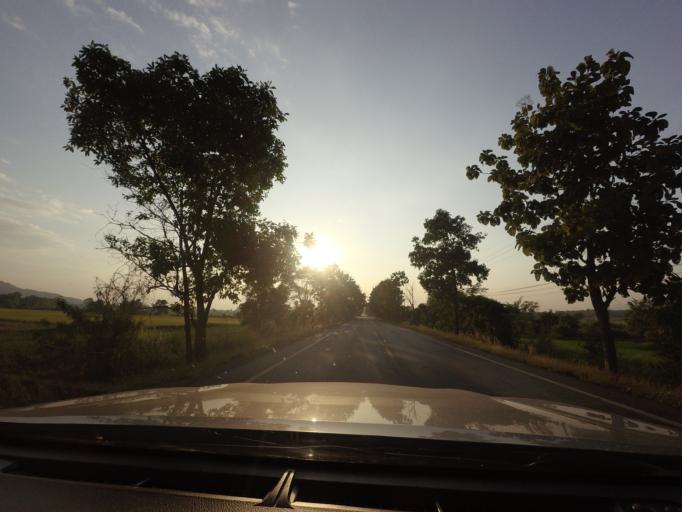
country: TH
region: Phitsanulok
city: Noen Maprang
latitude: 16.6936
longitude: 100.5522
